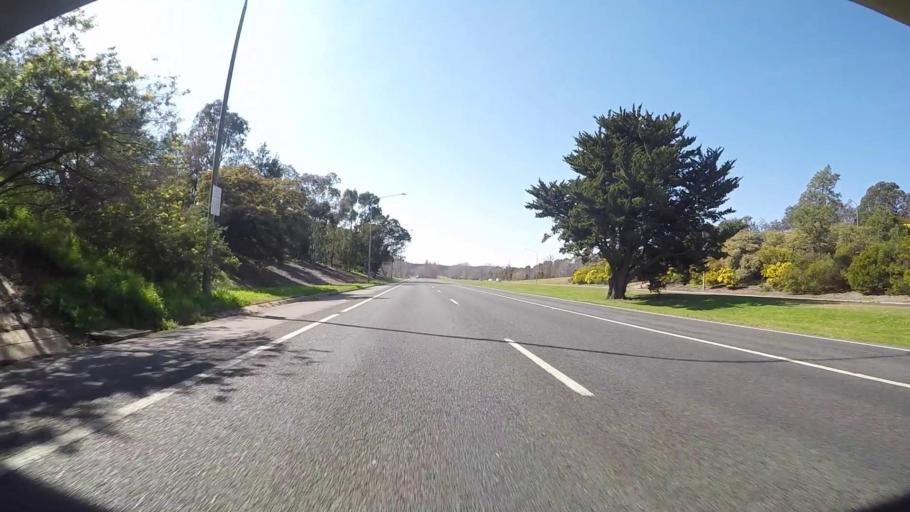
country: AU
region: Australian Capital Territory
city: Forrest
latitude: -35.3262
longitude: 149.0871
